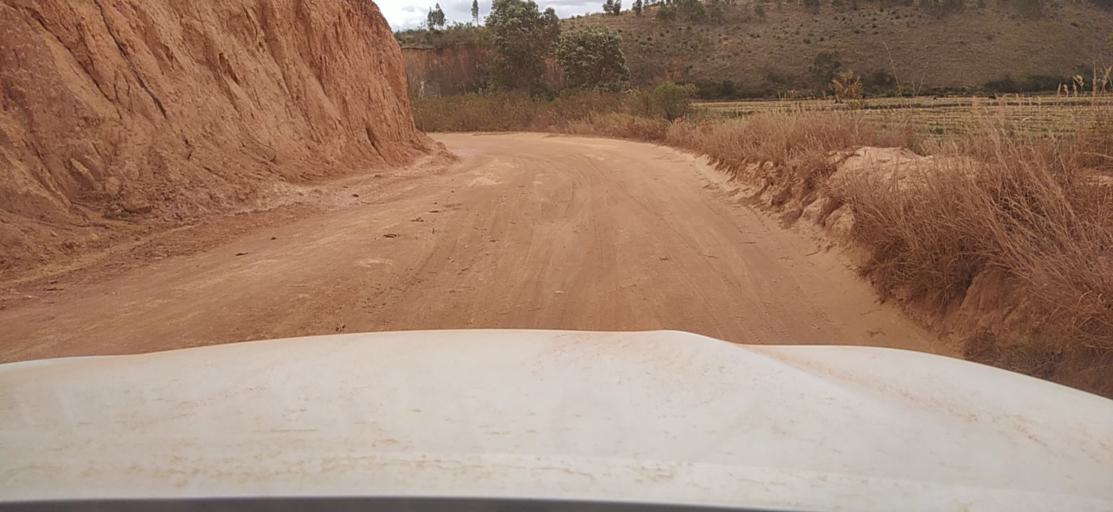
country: MG
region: Alaotra Mangoro
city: Ambatondrazaka
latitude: -18.0042
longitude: 48.2634
